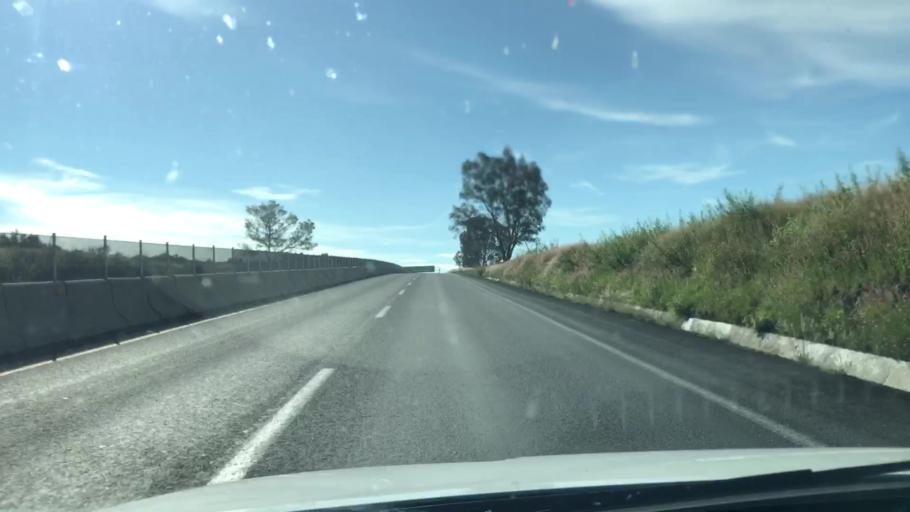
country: MX
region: Guanajuato
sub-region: Leon
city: Rizos de la Joya (Rizos del Saucillo)
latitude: 21.1220
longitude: -101.8100
